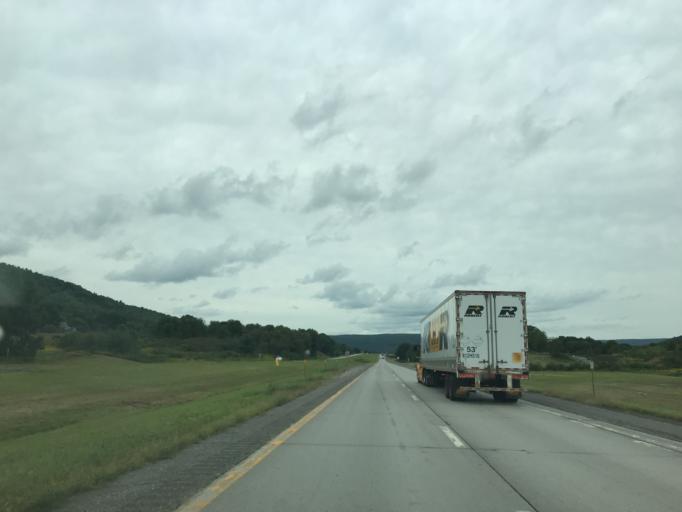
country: US
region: New York
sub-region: Otsego County
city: Oneonta
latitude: 42.4649
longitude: -75.0054
